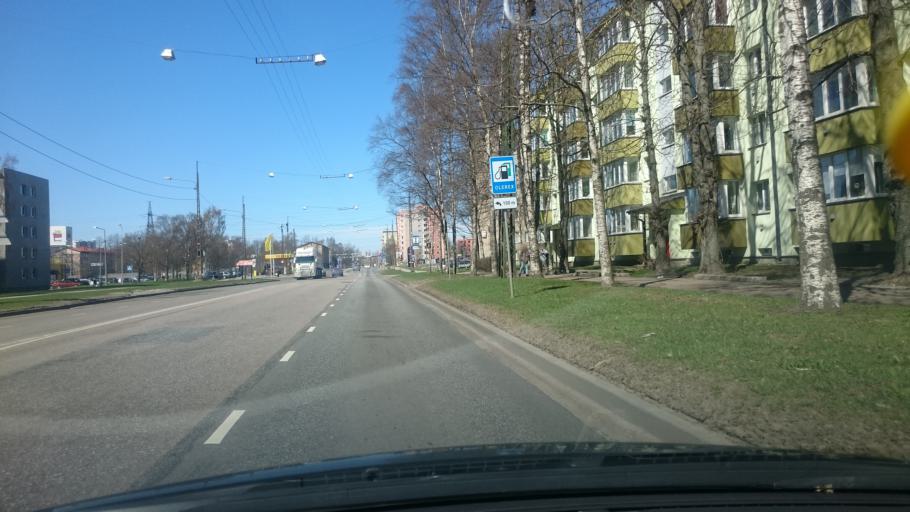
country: EE
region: Harju
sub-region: Tallinna linn
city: Tallinn
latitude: 59.4441
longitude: 24.7033
